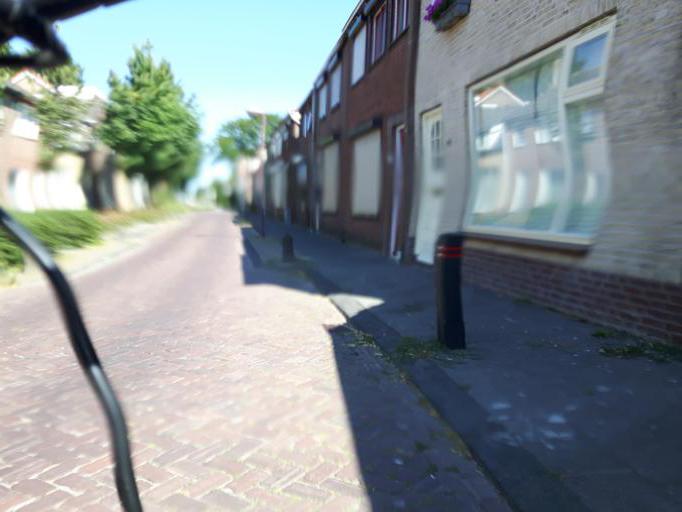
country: NL
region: North Brabant
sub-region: Gemeente Moerdijk
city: Klundert
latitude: 51.6665
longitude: 4.5361
